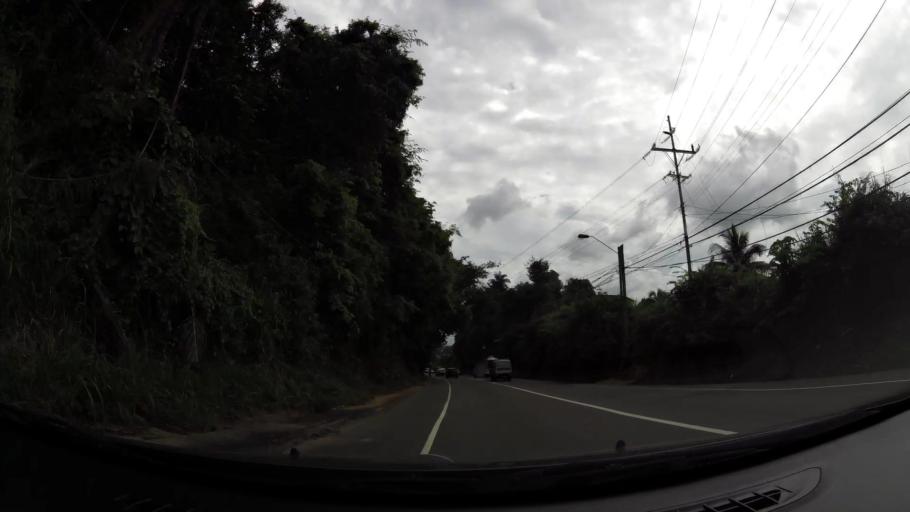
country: TT
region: San Juan/Laventille
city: Laventille
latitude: 10.6665
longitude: -61.4825
